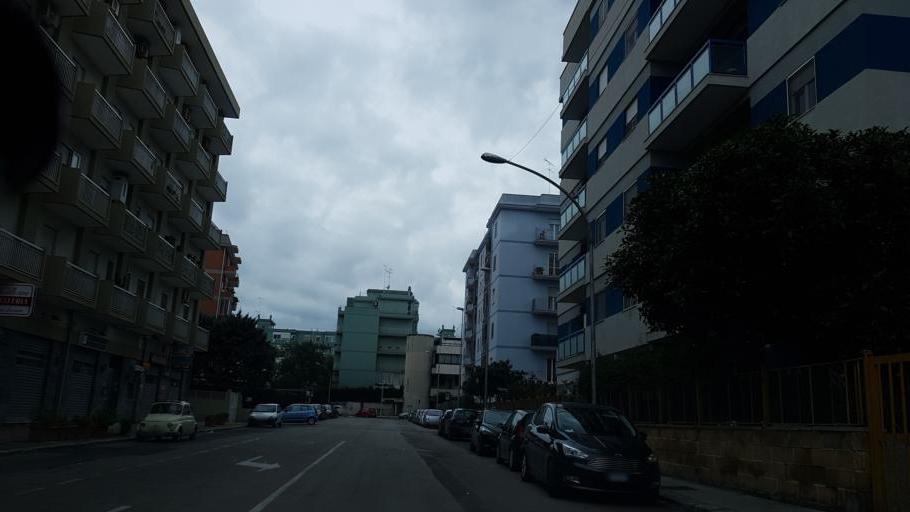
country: IT
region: Apulia
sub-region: Provincia di Brindisi
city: Brindisi
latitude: 40.6259
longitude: 17.9281
